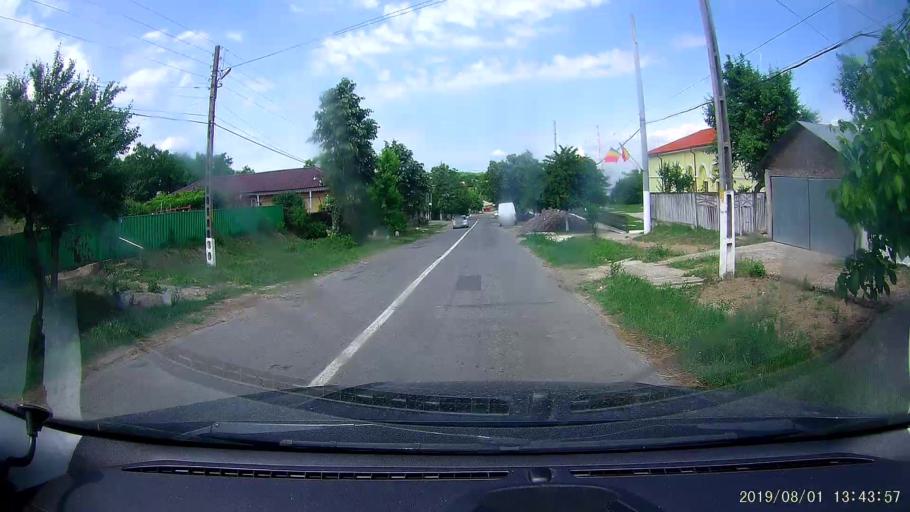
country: RO
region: Galati
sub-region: Comuna Oancea
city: Oancea
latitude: 45.9180
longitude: 28.1132
